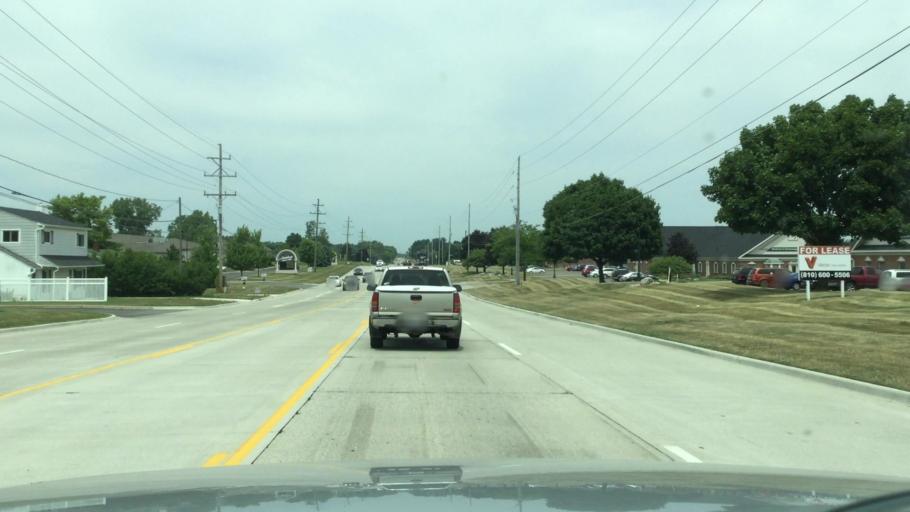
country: US
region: Michigan
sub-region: Genesee County
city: Swartz Creek
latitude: 43.0084
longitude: -83.7728
